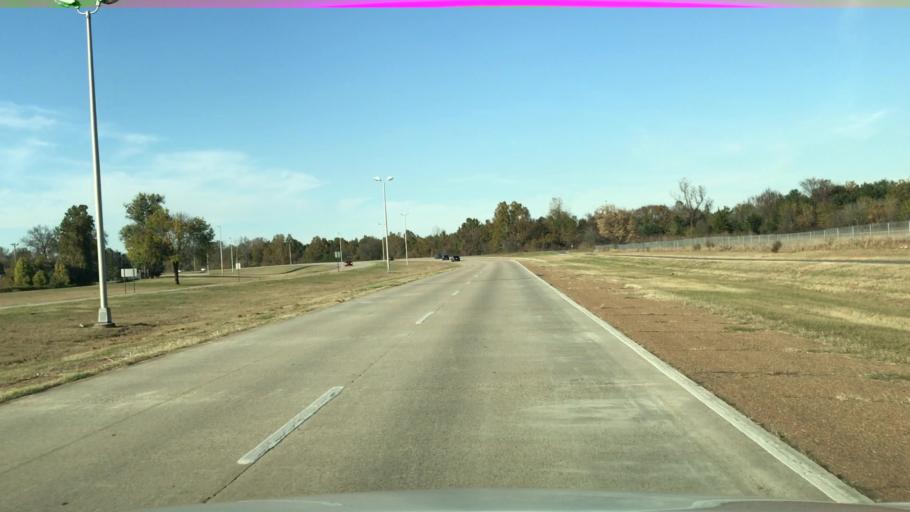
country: US
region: Louisiana
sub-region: Bossier Parish
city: Bossier City
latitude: 32.4816
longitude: -93.6931
